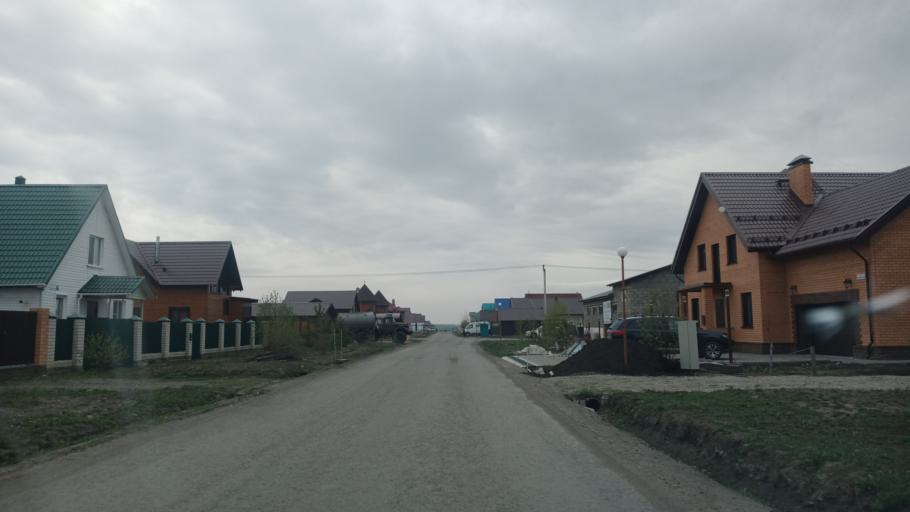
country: RU
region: Altai Krai
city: Yuzhnyy
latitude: 53.2237
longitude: 83.6905
